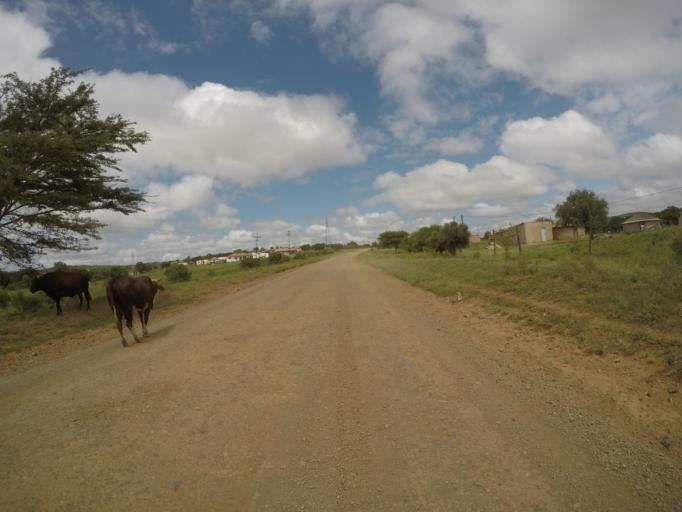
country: ZA
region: KwaZulu-Natal
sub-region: uThungulu District Municipality
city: Empangeni
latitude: -28.5904
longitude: 31.8413
